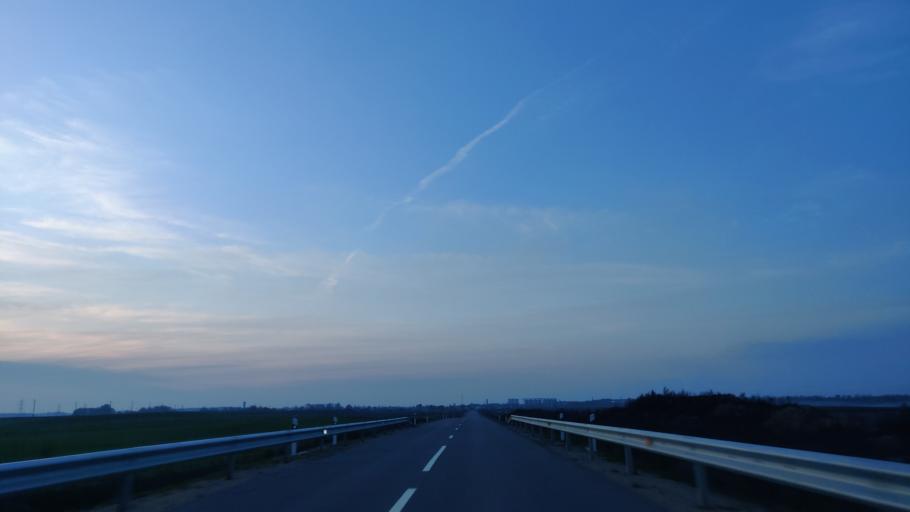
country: LT
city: Lentvaris
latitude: 54.6027
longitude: 25.0059
